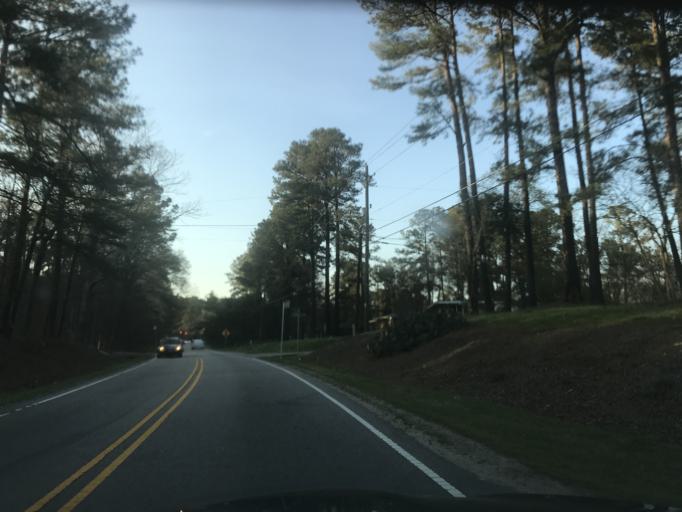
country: US
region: North Carolina
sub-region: Wake County
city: Knightdale
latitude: 35.7522
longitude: -78.5352
